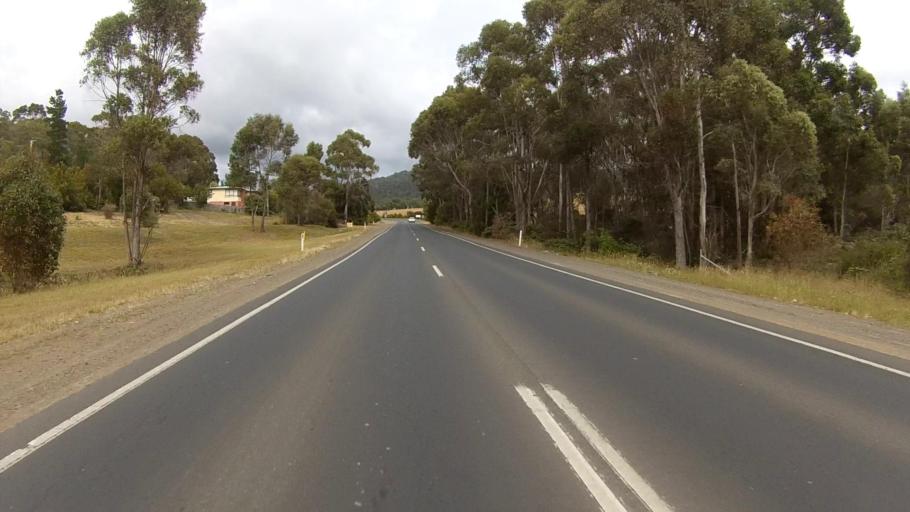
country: AU
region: Tasmania
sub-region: Kingborough
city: Margate
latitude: -43.0554
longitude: 147.2598
